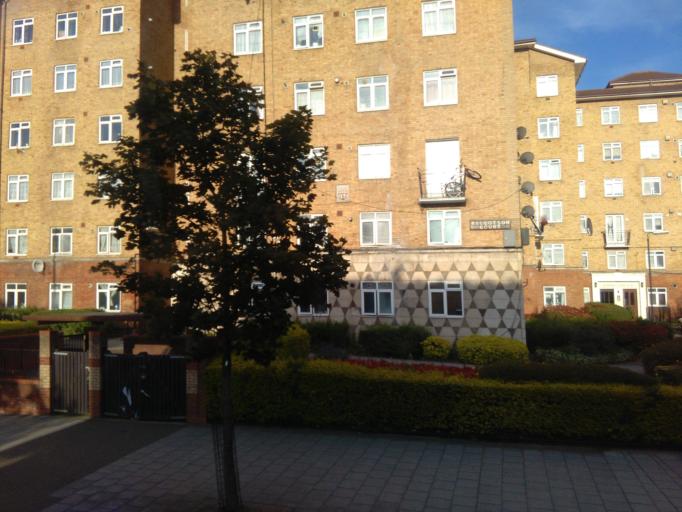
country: GB
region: England
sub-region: Greater London
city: Battersea
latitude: 51.4770
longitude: -0.1301
